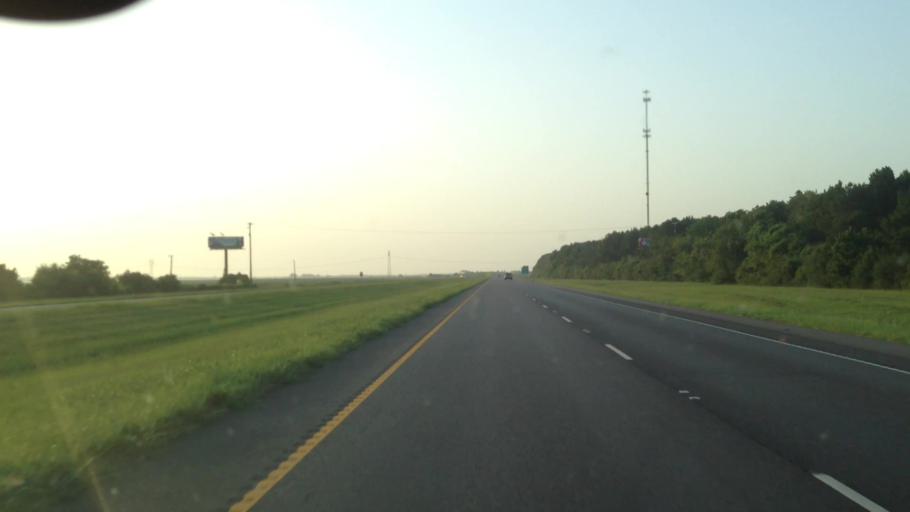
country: US
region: Louisiana
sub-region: Red River Parish
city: Coushatta
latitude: 31.8442
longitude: -93.2898
